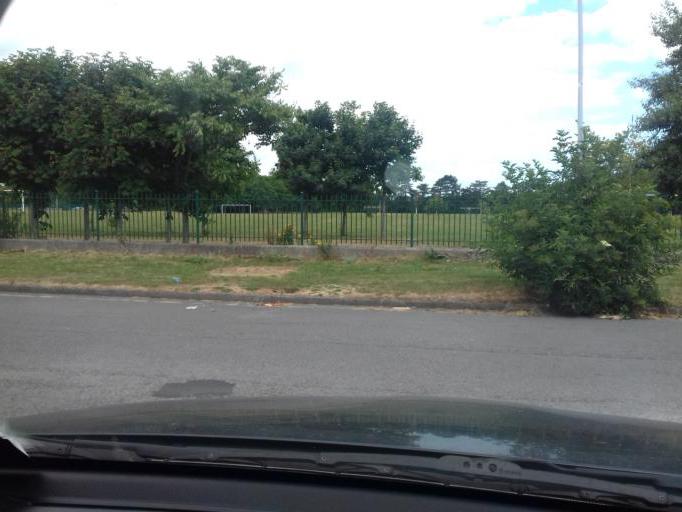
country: IE
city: Bonnybrook
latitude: 53.4060
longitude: -6.2142
